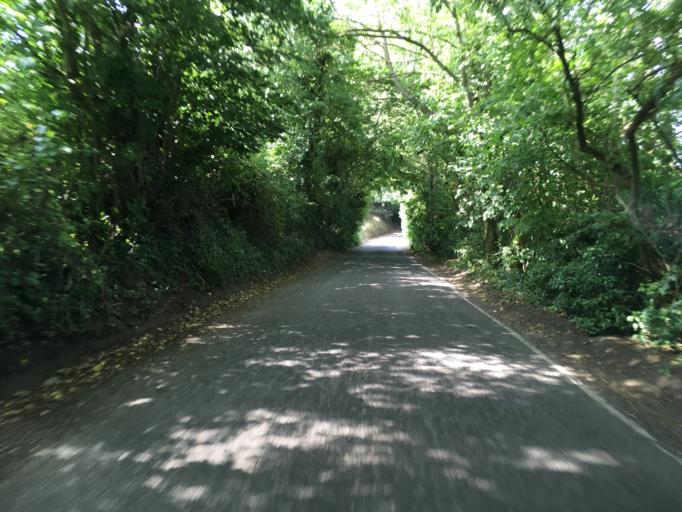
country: GB
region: England
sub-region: Kent
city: Maidstone
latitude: 51.2425
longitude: 0.5120
